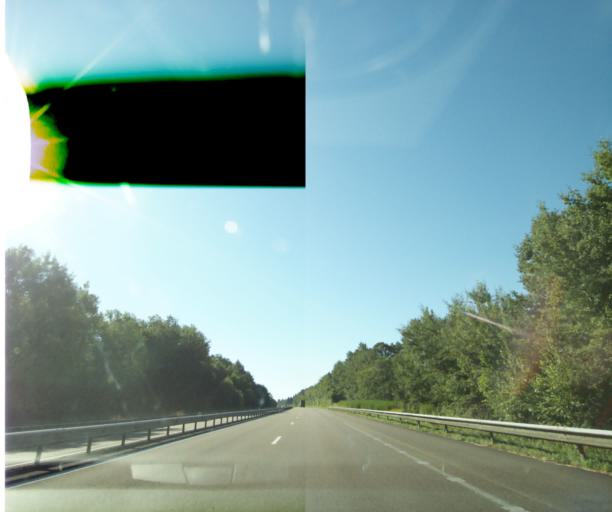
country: FR
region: Champagne-Ardenne
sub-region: Departement de l'Aube
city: Lusigny-sur-Barse
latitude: 48.1850
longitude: 4.2835
